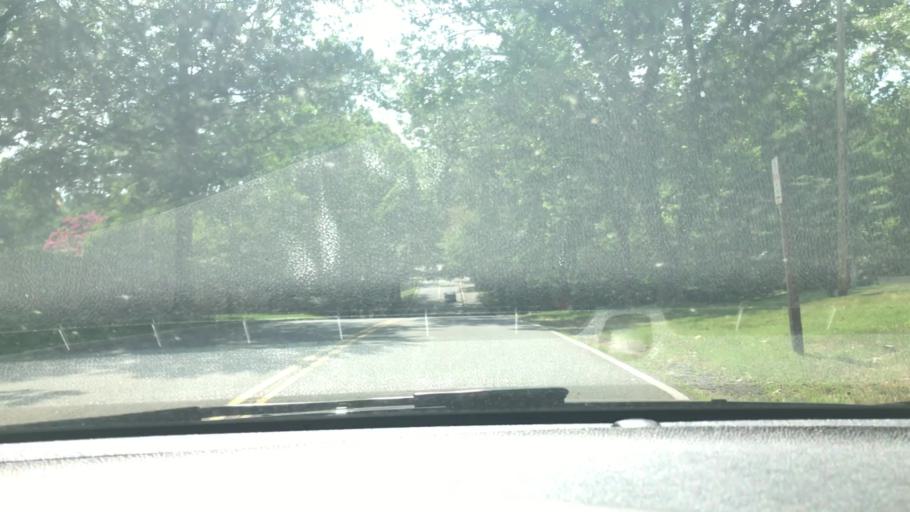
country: US
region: Washington, D.C.
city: Washington, D.C.
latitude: 38.8879
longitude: -77.0690
